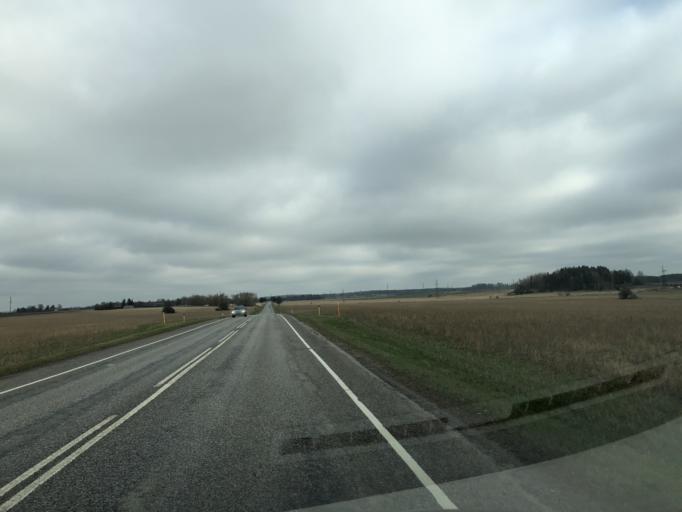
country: EE
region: Laeaene-Virumaa
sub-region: Rakvere linn
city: Rakvere
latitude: 59.2975
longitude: 26.3137
